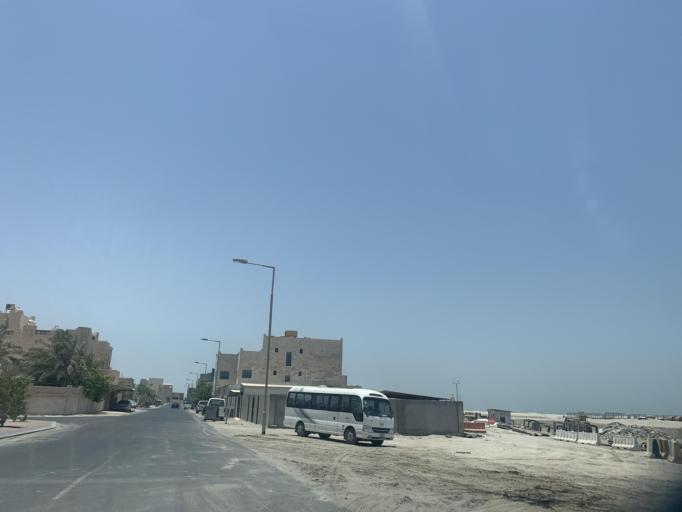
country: BH
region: Muharraq
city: Al Muharraq
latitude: 26.2877
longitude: 50.6217
